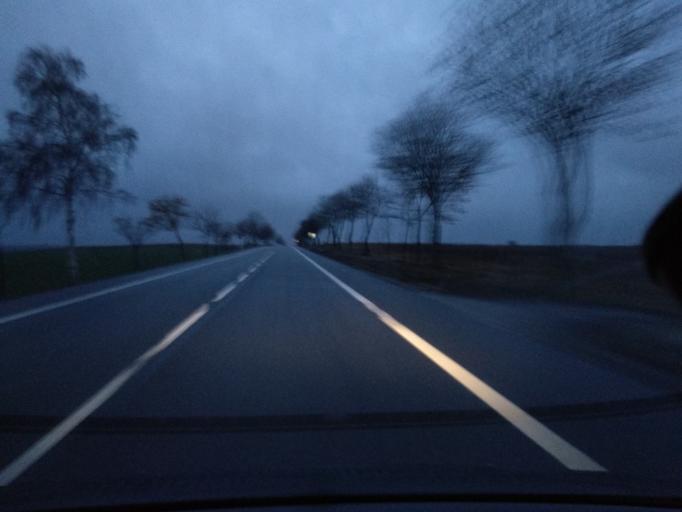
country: PL
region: Lower Silesian Voivodeship
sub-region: Powiat sredzki
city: Miekinia
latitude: 51.1606
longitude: 16.7075
